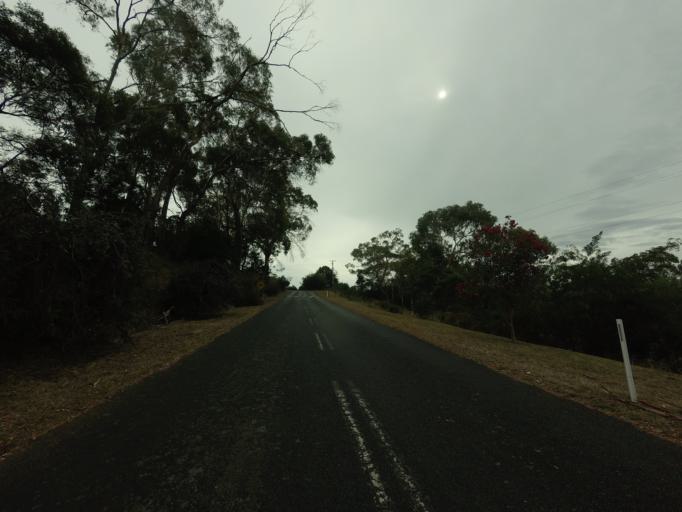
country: AU
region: Tasmania
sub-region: Clarence
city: Seven Mile Beach
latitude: -42.8193
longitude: 147.5082
